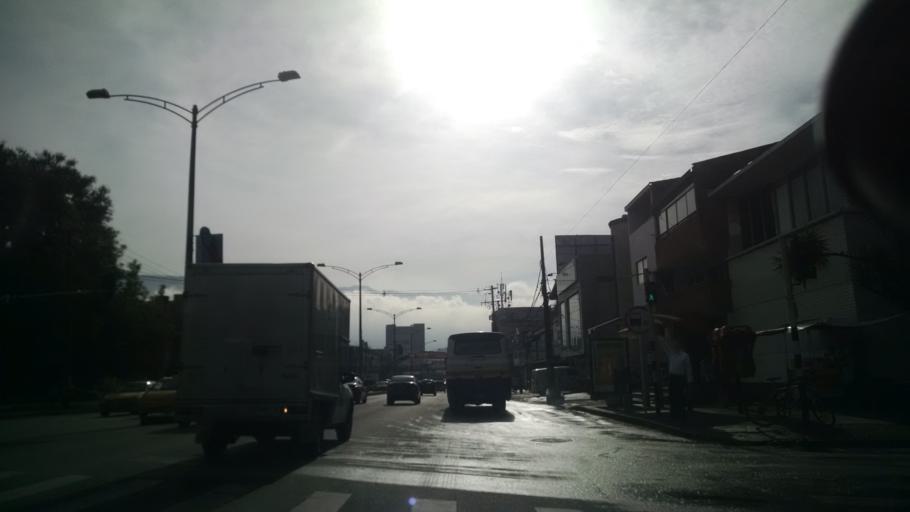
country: CO
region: Antioquia
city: Medellin
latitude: 6.2392
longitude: -75.5867
